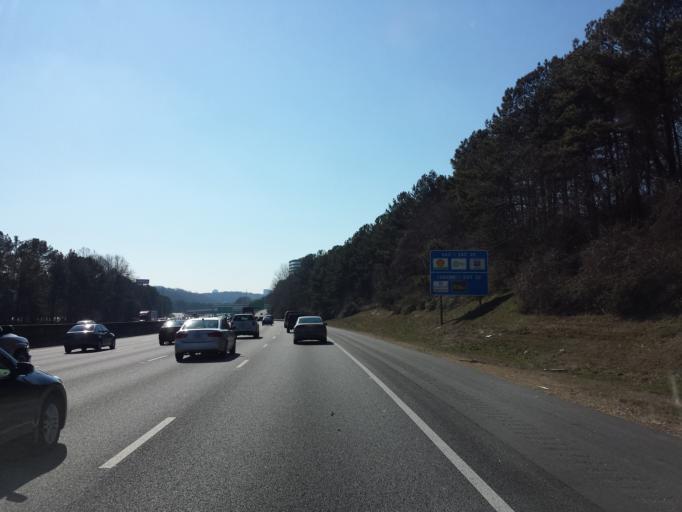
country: US
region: Georgia
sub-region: Fulton County
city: Sandy Springs
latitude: 33.9135
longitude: -84.4239
